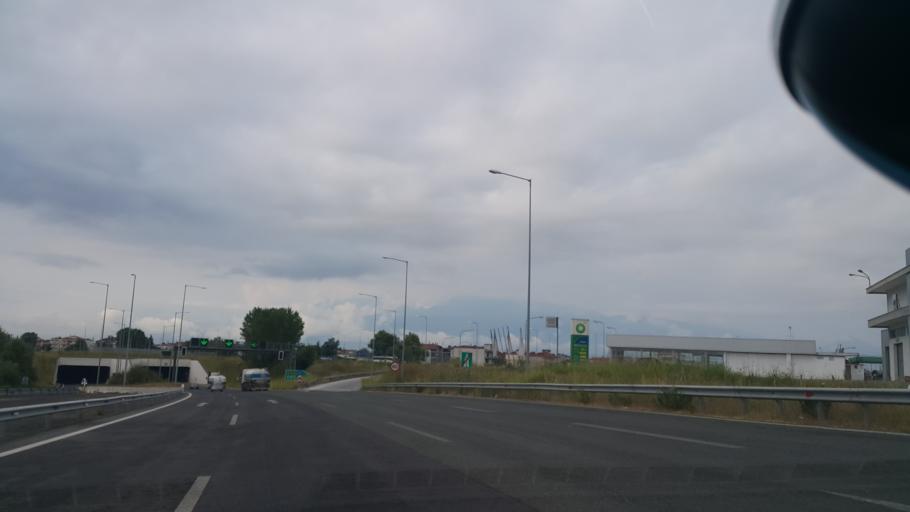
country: GR
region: Central Macedonia
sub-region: Nomos Pierias
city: Katerini
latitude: 40.2781
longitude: 22.5216
